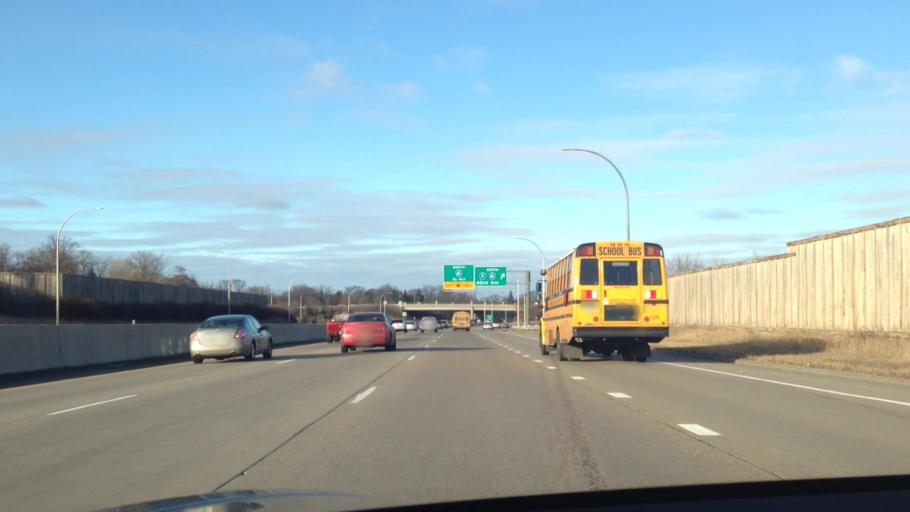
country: US
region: Minnesota
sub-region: Hennepin County
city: Robbinsdale
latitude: 45.0268
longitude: -93.3473
